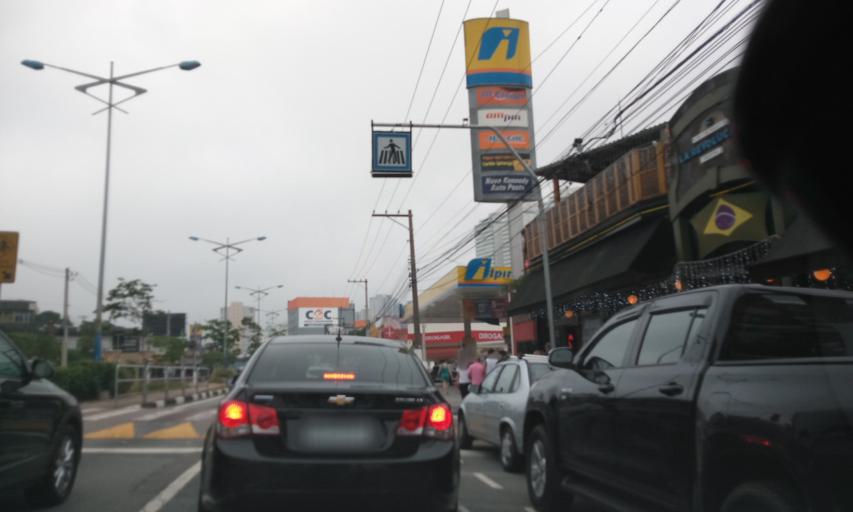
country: BR
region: Sao Paulo
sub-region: Sao Bernardo Do Campo
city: Sao Bernardo do Campo
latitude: -23.6833
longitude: -46.5581
